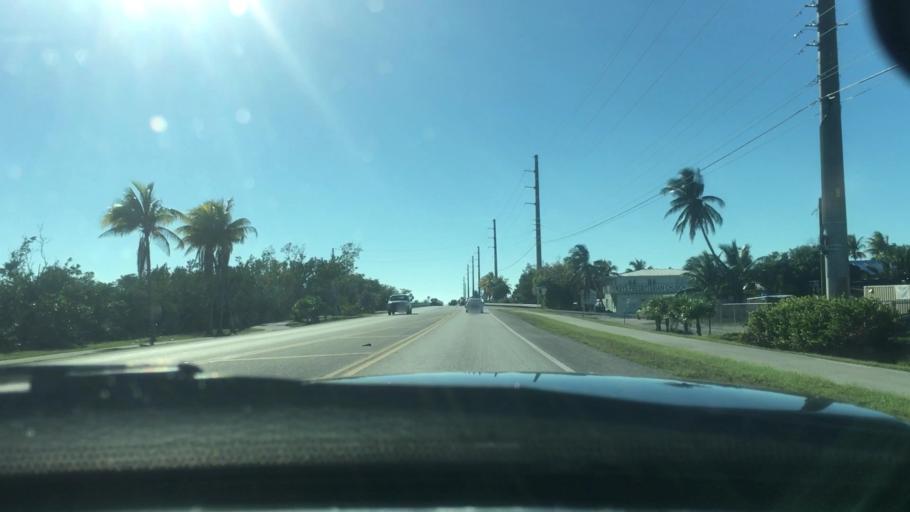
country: US
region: Florida
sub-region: Monroe County
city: Big Coppitt Key
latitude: 24.5942
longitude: -81.6632
